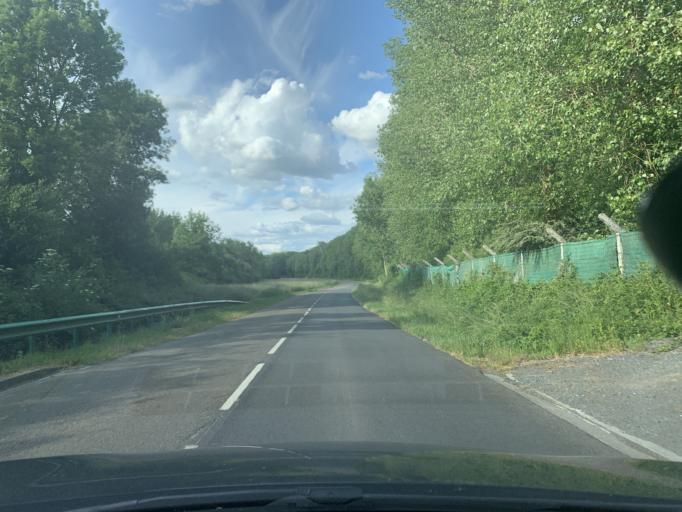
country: FR
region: Nord-Pas-de-Calais
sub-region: Departement du Nord
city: Gouzeaucourt
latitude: 50.0846
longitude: 3.1424
